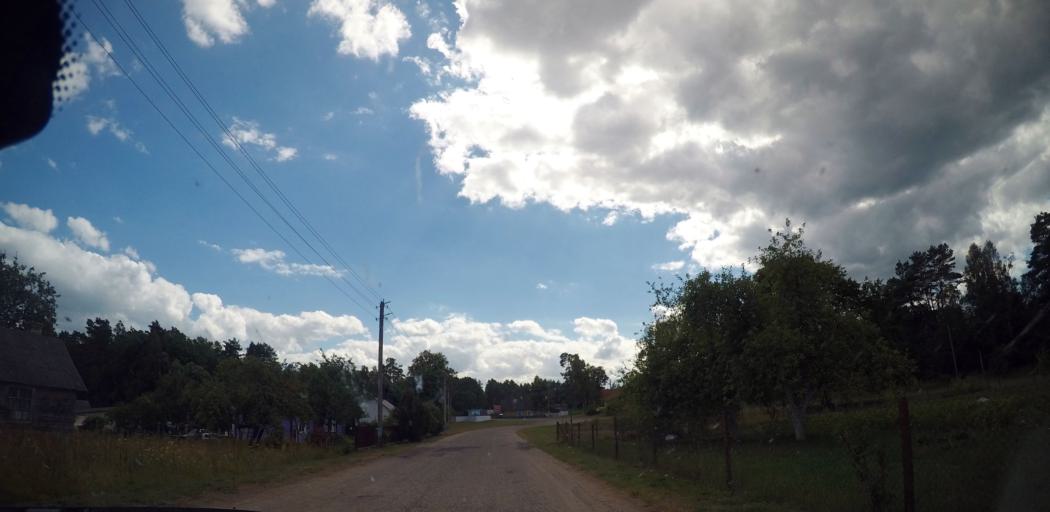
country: BY
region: Grodnenskaya
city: Skidal'
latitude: 53.8189
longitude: 24.2450
